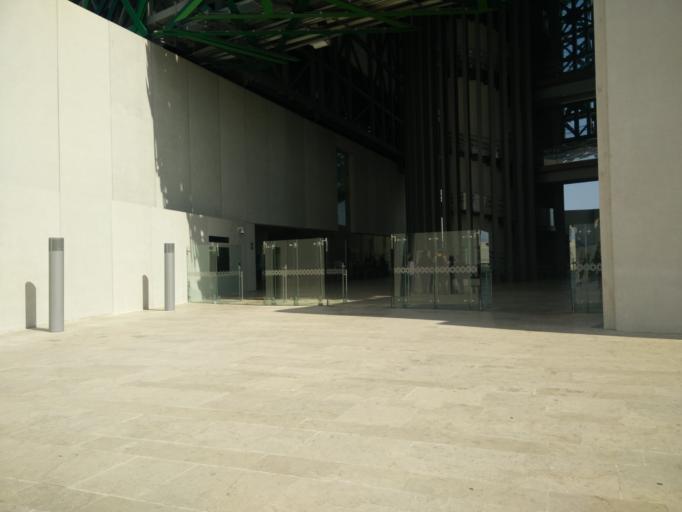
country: MX
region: Yucatan
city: Merida
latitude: 21.0347
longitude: -89.6284
